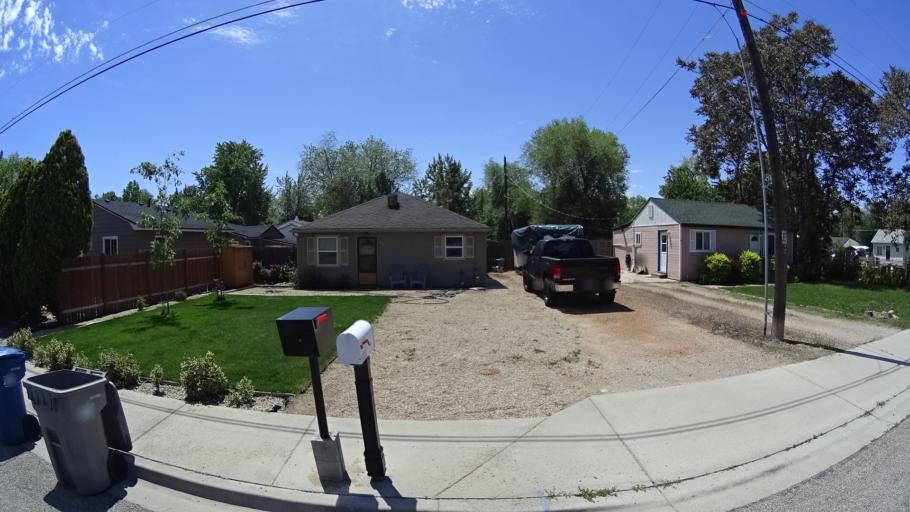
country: US
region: Idaho
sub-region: Ada County
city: Boise
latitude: 43.6043
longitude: -116.2241
